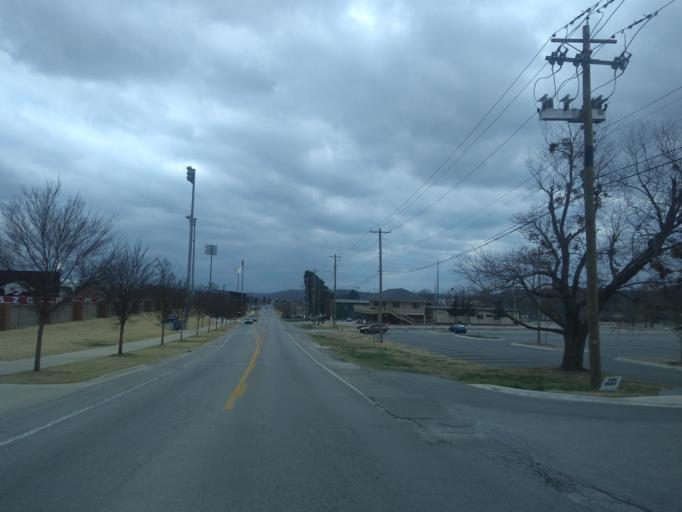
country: US
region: Arkansas
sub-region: Washington County
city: Fayetteville
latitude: 36.0655
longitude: -94.1801
